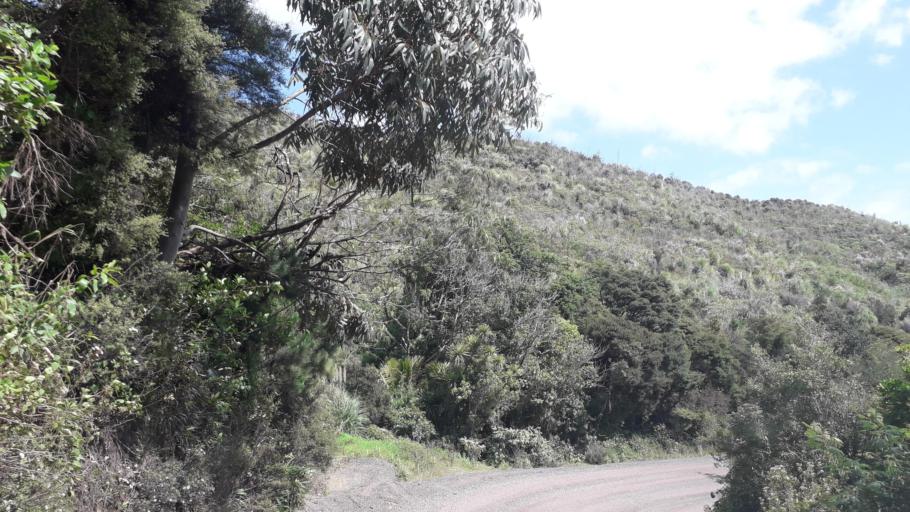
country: NZ
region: Northland
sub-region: Far North District
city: Paihia
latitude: -35.2391
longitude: 174.2543
